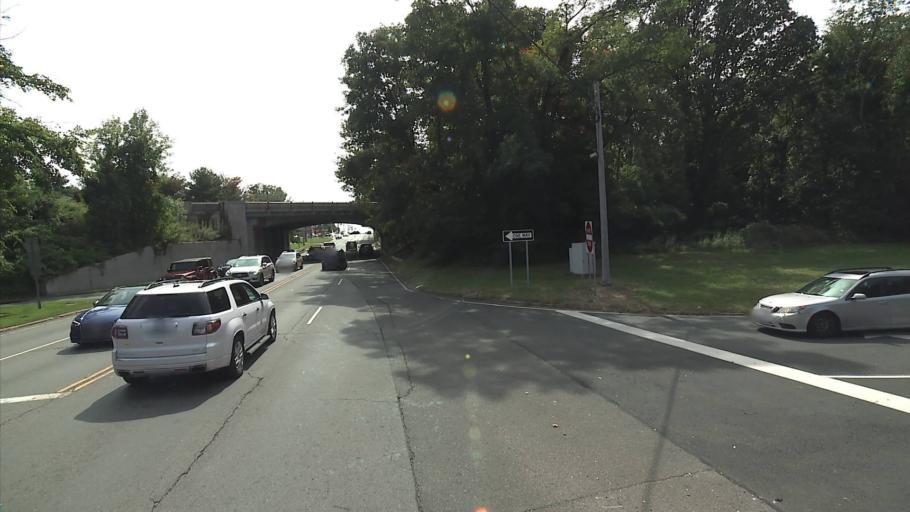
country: US
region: Connecticut
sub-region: Fairfield County
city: North Stamford
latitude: 41.1126
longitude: -73.5464
